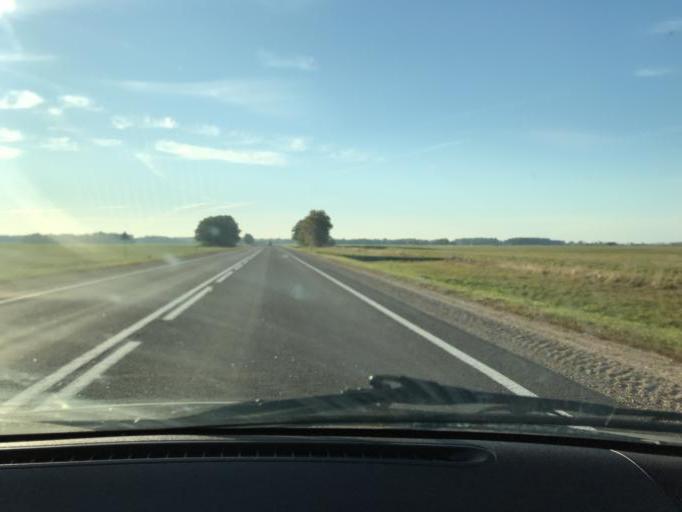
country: BY
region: Brest
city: Antopal'
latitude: 52.2071
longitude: 24.5953
